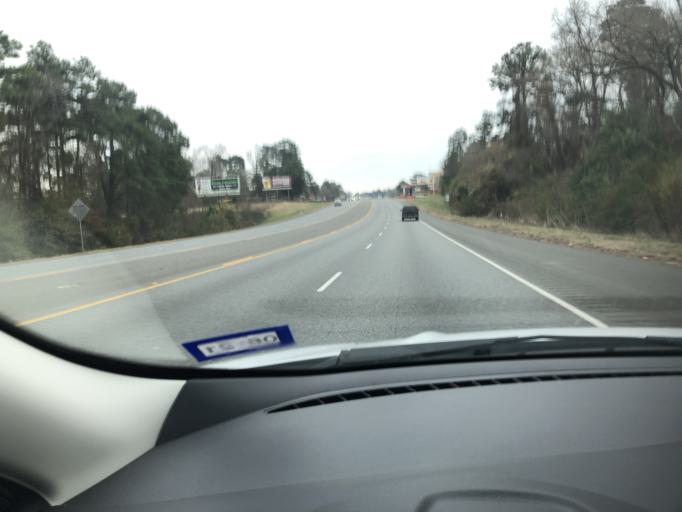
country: US
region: Texas
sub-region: Angelina County
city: Redland
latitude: 31.3998
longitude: -94.7191
